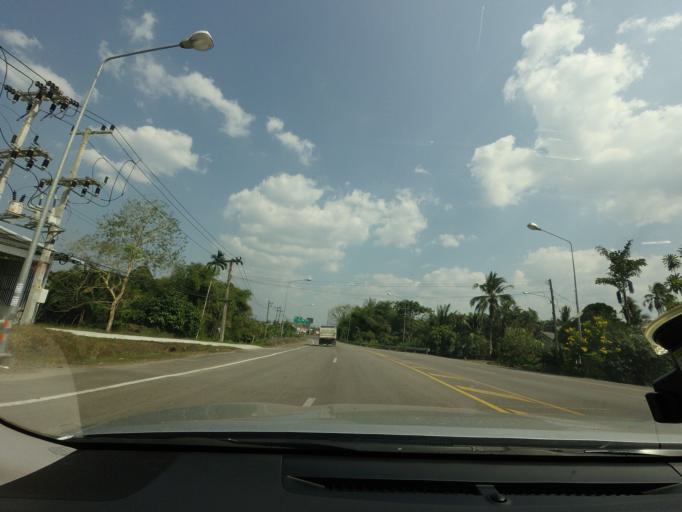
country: TH
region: Phangnga
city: Thap Put
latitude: 8.5221
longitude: 98.6331
